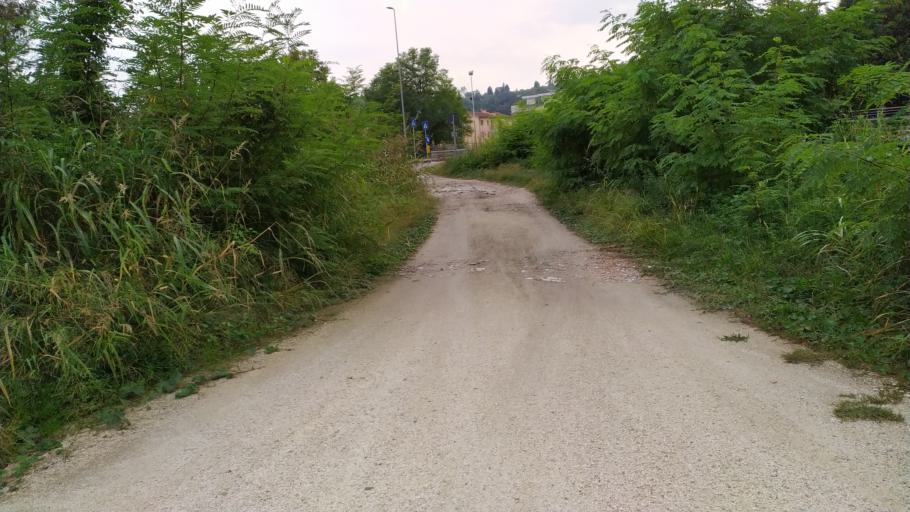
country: IT
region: Veneto
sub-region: Provincia di Treviso
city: Conegliano
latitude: 45.8996
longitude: 12.2953
